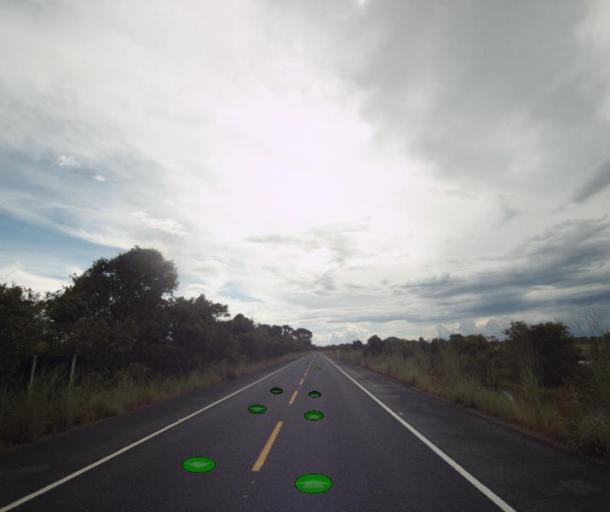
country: BR
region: Goias
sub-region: Sao Miguel Do Araguaia
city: Sao Miguel do Araguaia
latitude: -13.2353
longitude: -50.5578
